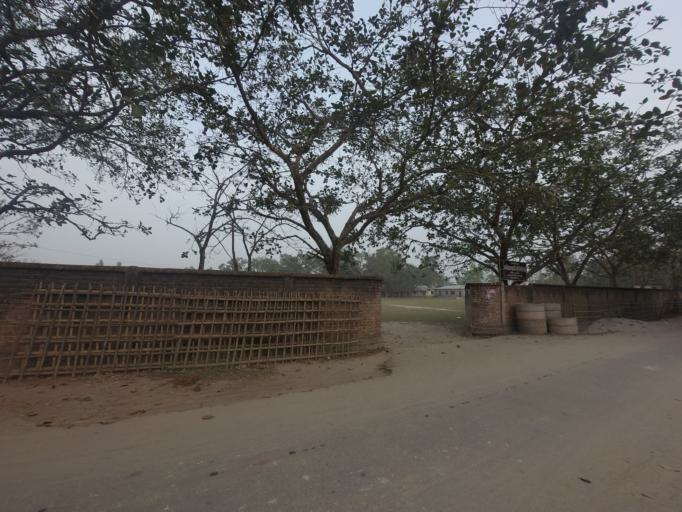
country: BD
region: Rajshahi
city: Saidpur
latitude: 25.9106
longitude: 88.8920
